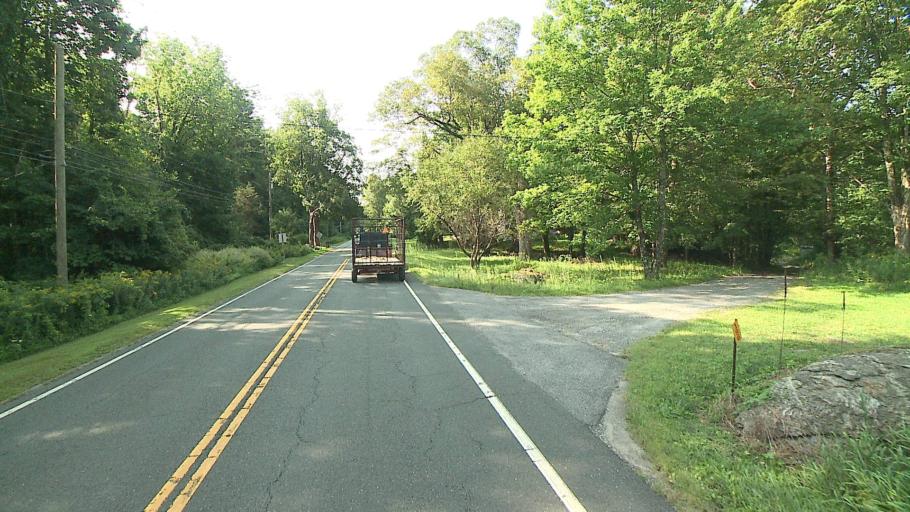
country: US
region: Connecticut
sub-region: Litchfield County
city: Canaan
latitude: 41.9436
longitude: -73.3594
